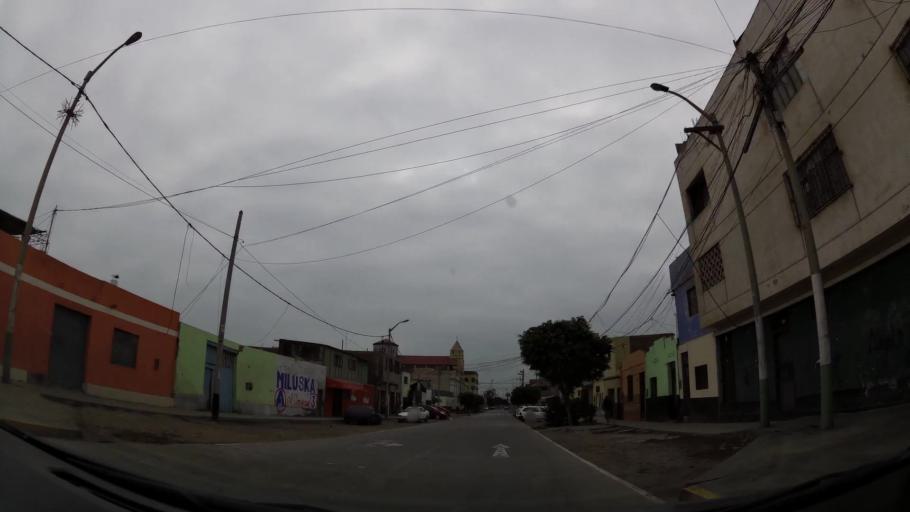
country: PE
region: Callao
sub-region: Callao
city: Callao
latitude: -12.0547
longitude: -77.1365
